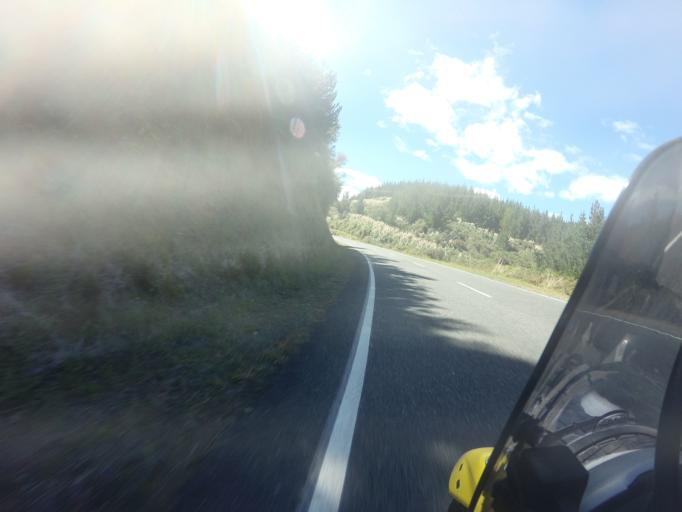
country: NZ
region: Bay of Plenty
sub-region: Whakatane District
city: Murupara
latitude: -38.2843
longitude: 176.8153
